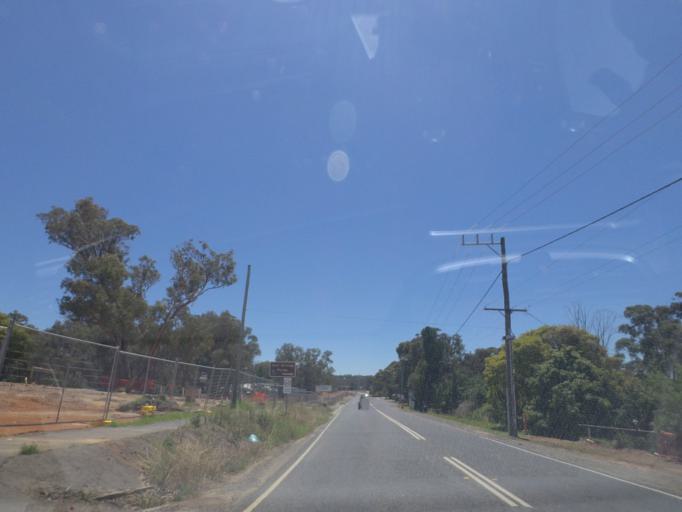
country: AU
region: Victoria
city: Plenty
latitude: -37.6630
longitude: 145.1237
